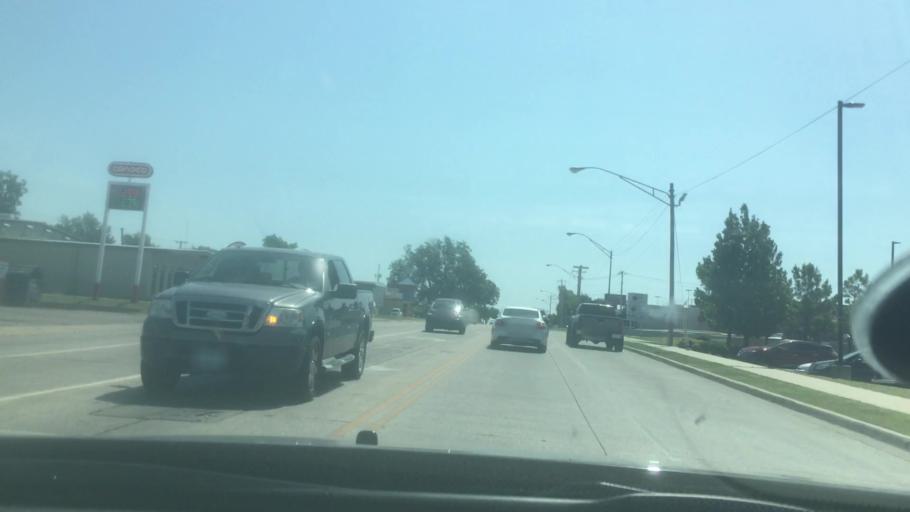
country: US
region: Oklahoma
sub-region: Pontotoc County
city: Ada
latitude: 34.7816
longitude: -96.6634
